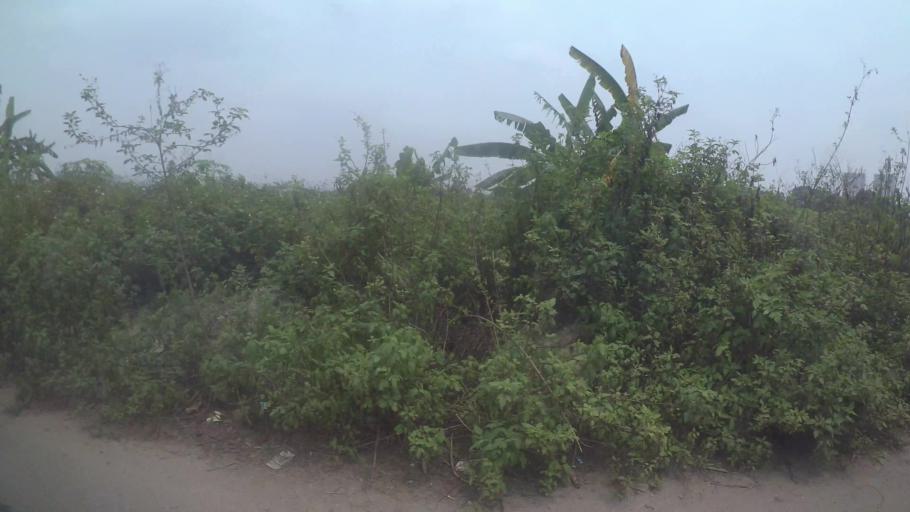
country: VN
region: Ha Noi
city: Cau Dien
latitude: 21.0239
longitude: 105.7456
